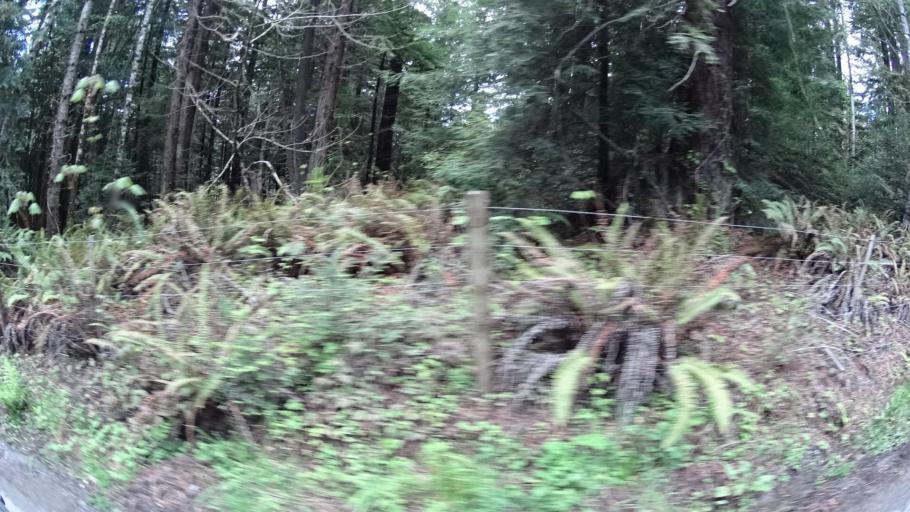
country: US
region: California
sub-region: Humboldt County
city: Blue Lake
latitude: 40.9059
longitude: -123.9753
